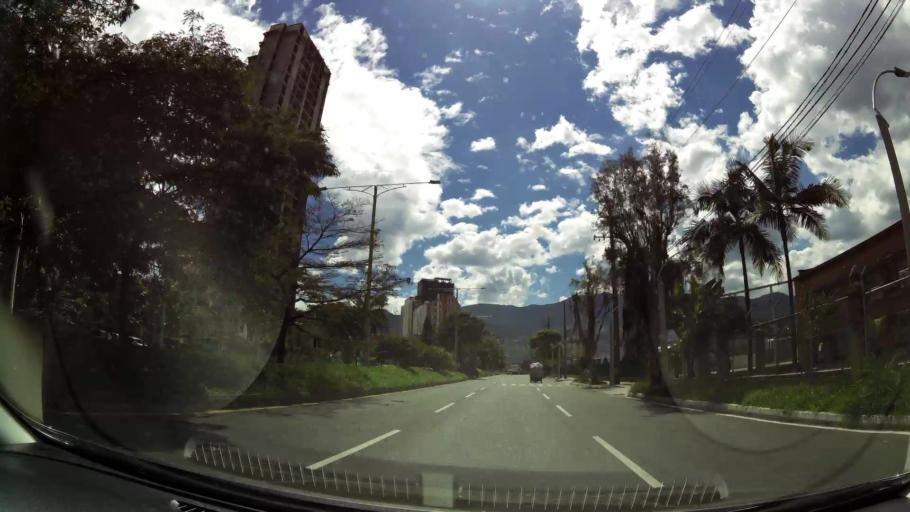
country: CO
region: Antioquia
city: Sabaneta
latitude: 6.1552
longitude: -75.6140
